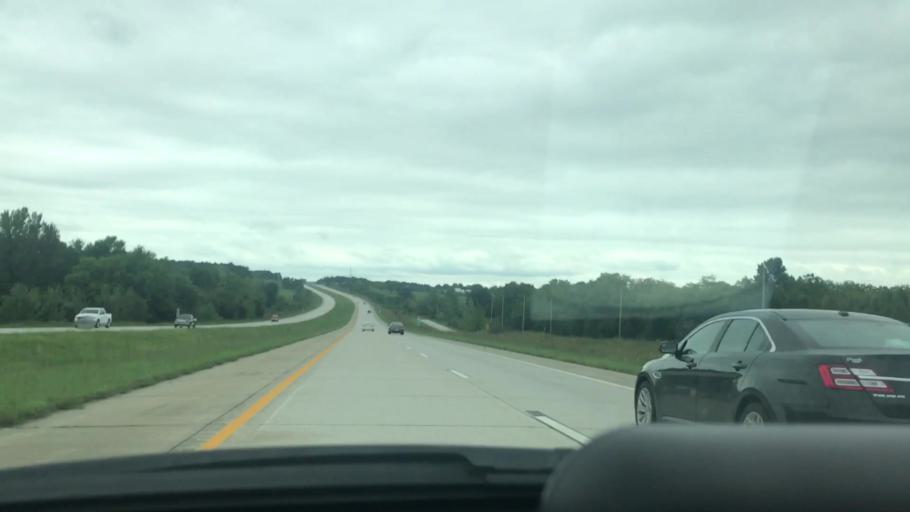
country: US
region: Missouri
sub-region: Dallas County
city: Buffalo
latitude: 37.5252
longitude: -93.1377
